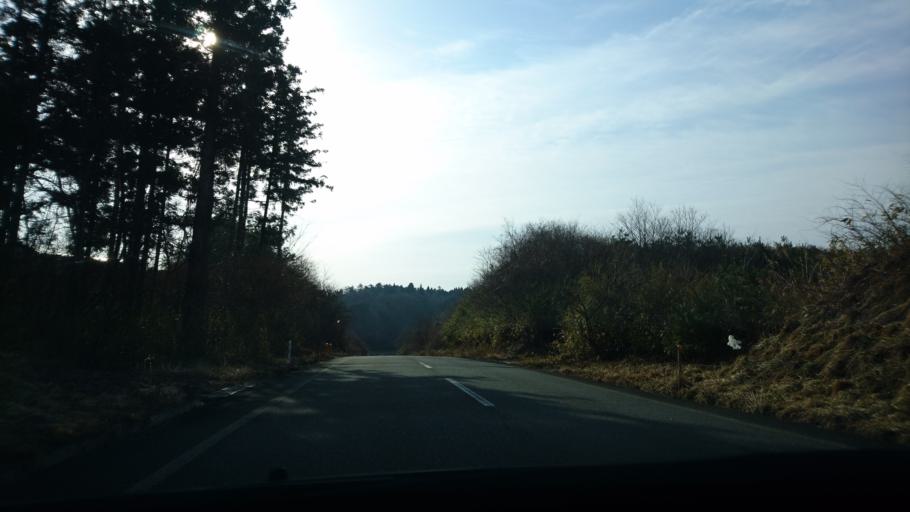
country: JP
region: Iwate
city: Ichinoseki
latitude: 38.8631
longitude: 141.1954
